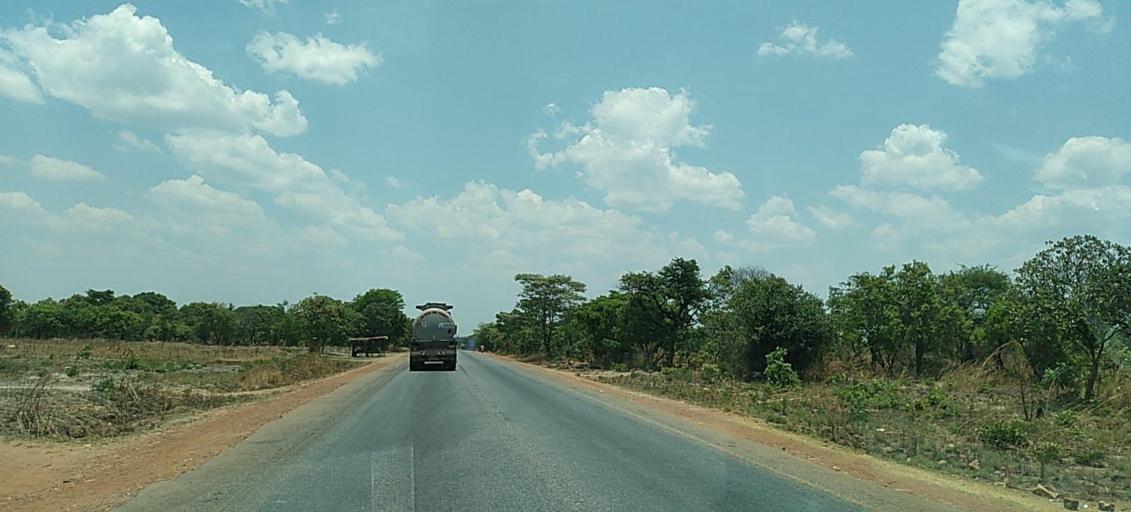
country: ZM
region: Central
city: Kapiri Mposhi
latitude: -13.7708
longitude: 28.6443
